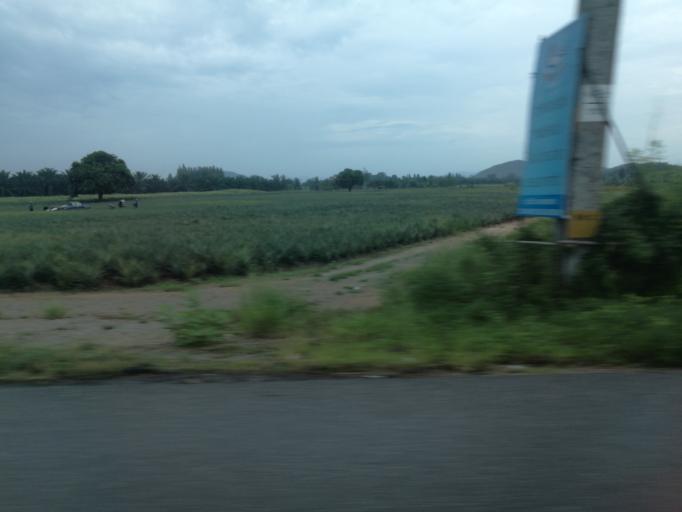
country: TH
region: Prachuap Khiri Khan
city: Kui Buri
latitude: 11.9664
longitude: 99.8311
